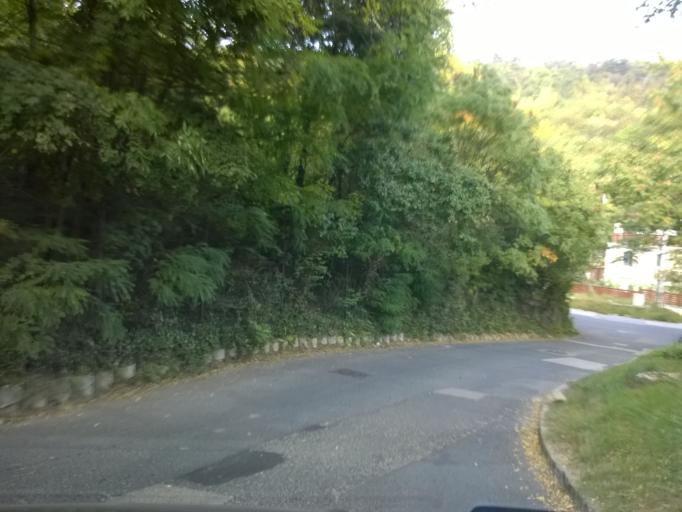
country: HU
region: Budapest
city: Budapest II. keruelet
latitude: 47.5373
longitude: 19.0133
